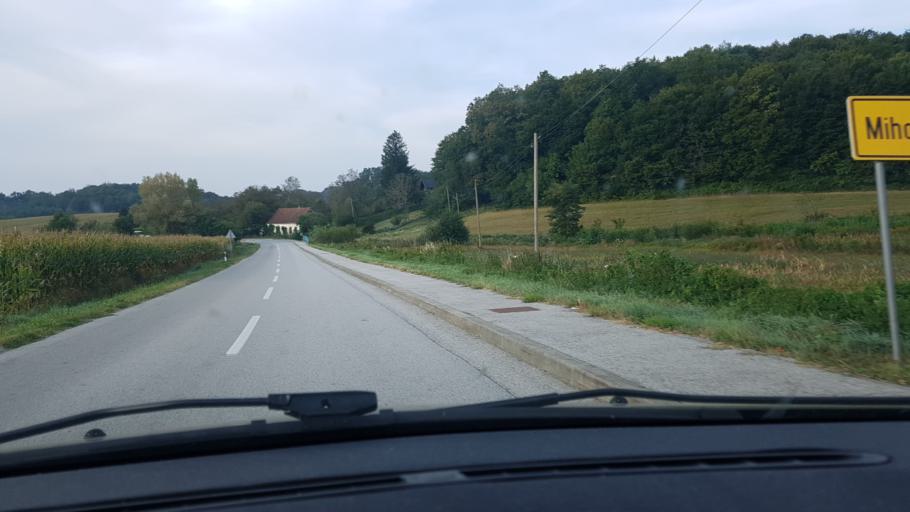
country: HR
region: Krapinsko-Zagorska
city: Mihovljan
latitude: 46.1506
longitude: 15.9604
